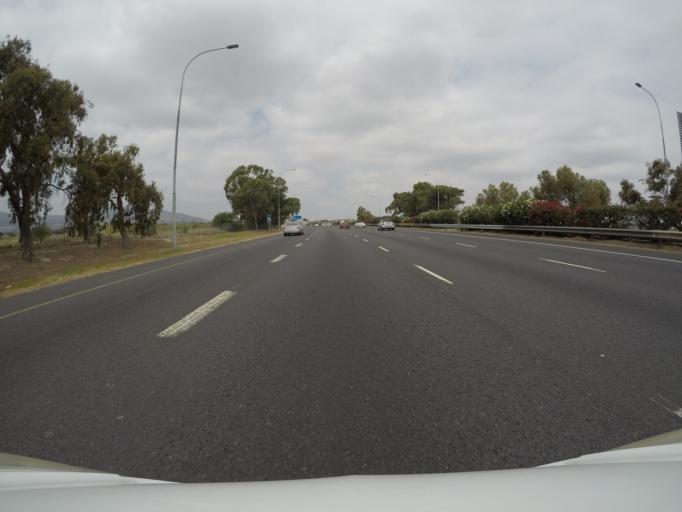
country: ZA
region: Western Cape
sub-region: City of Cape Town
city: Sunset Beach
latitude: -33.8903
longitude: 18.5452
